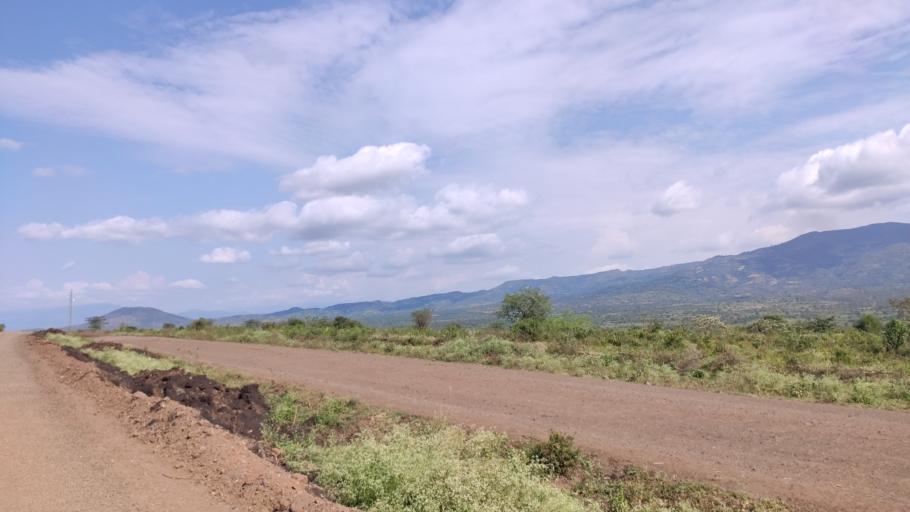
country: ET
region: Southern Nations, Nationalities, and People's Region
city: Felege Neway
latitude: 6.3953
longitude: 37.1050
